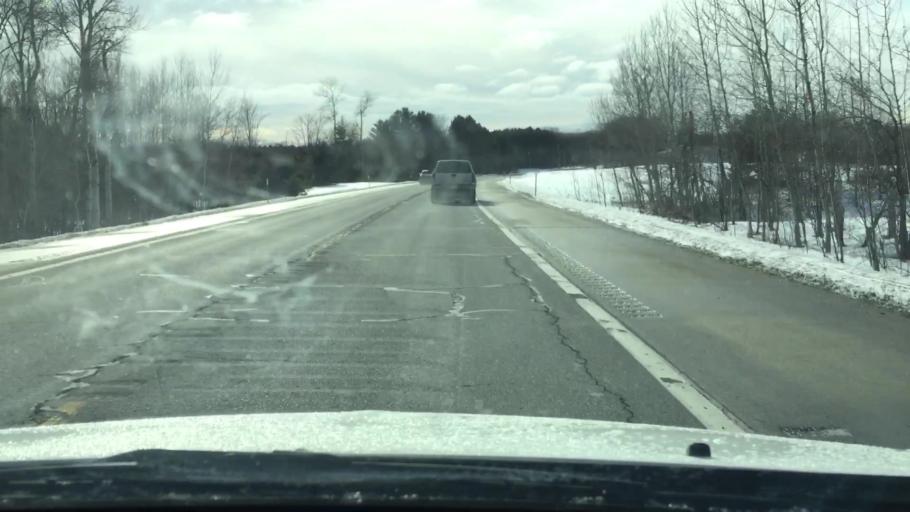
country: US
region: Michigan
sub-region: Wexford County
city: Manton
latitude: 44.5914
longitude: -85.3380
